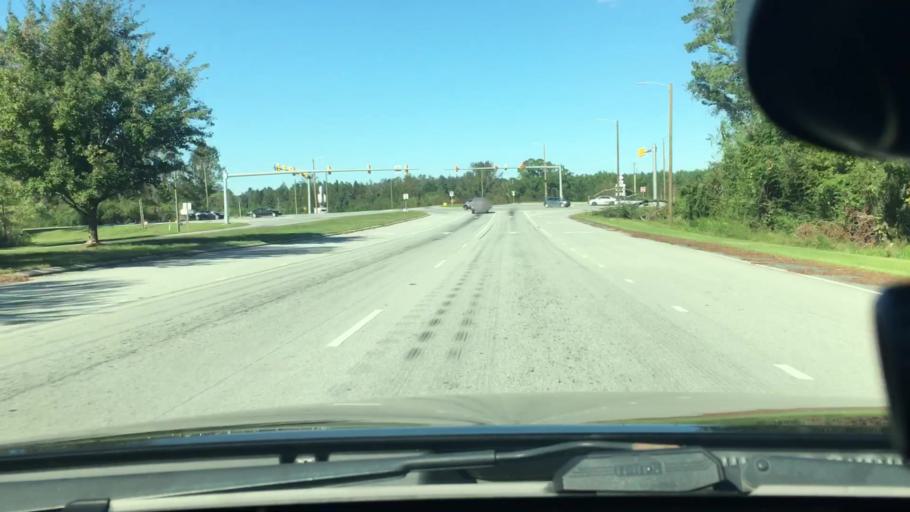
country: US
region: North Carolina
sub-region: Craven County
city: Trent Woods
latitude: 35.1431
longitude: -77.1071
